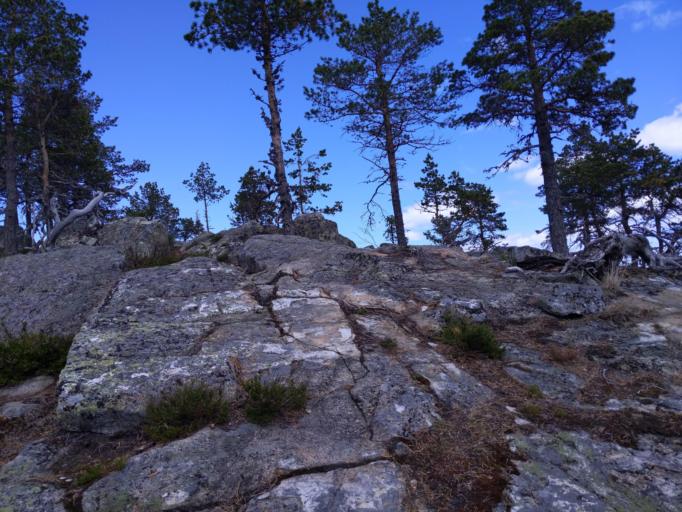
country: SE
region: Vaesternorrland
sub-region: OErnskoeldsviks Kommun
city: Kopmanholmen
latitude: 63.1767
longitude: 18.6828
